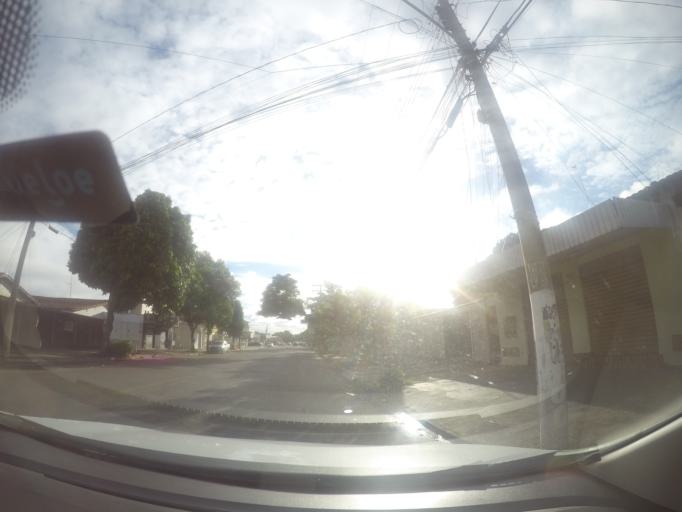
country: BR
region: Goias
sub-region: Goiania
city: Goiania
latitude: -16.6876
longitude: -49.3129
